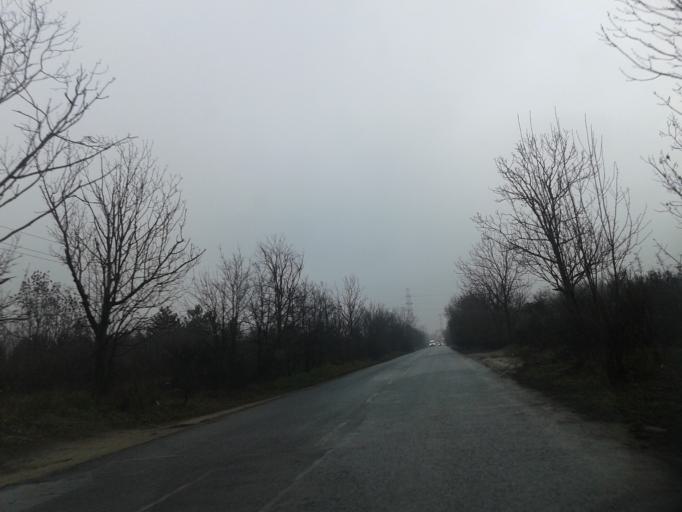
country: HU
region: Pest
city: Diosd
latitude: 47.4210
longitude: 18.9799
